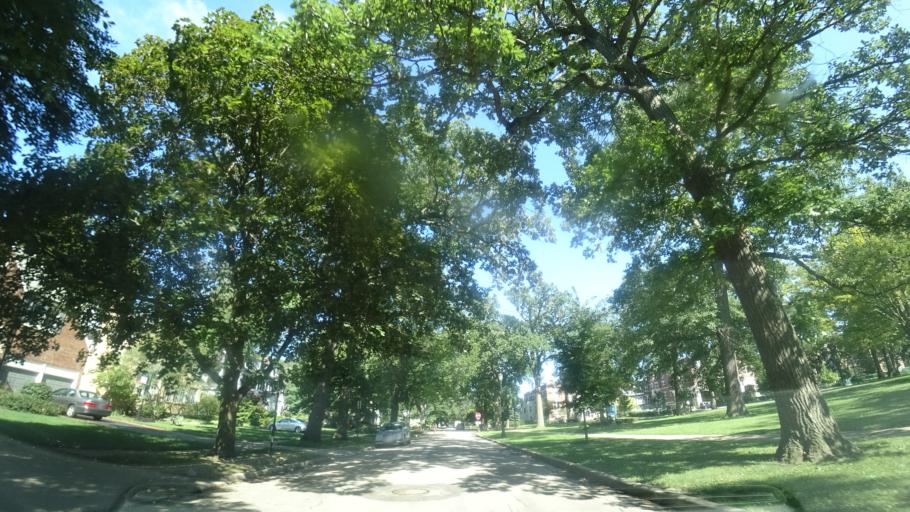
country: US
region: Illinois
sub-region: Cook County
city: Wilmette
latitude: 42.0607
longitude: -87.7090
